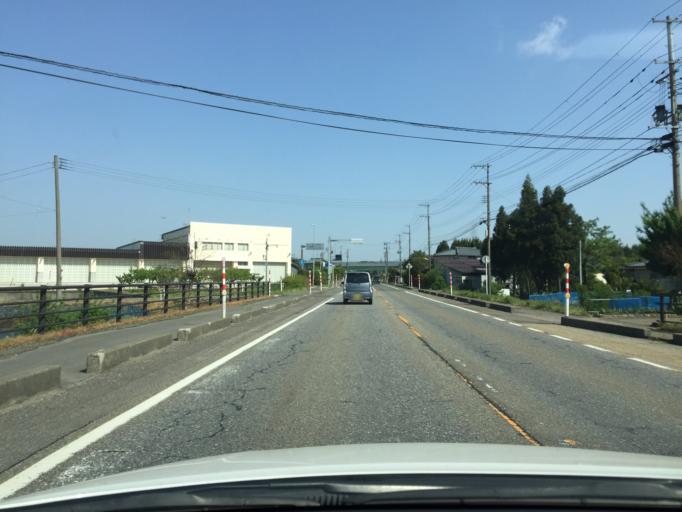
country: JP
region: Niigata
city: Gosen
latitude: 37.7498
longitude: 139.2518
